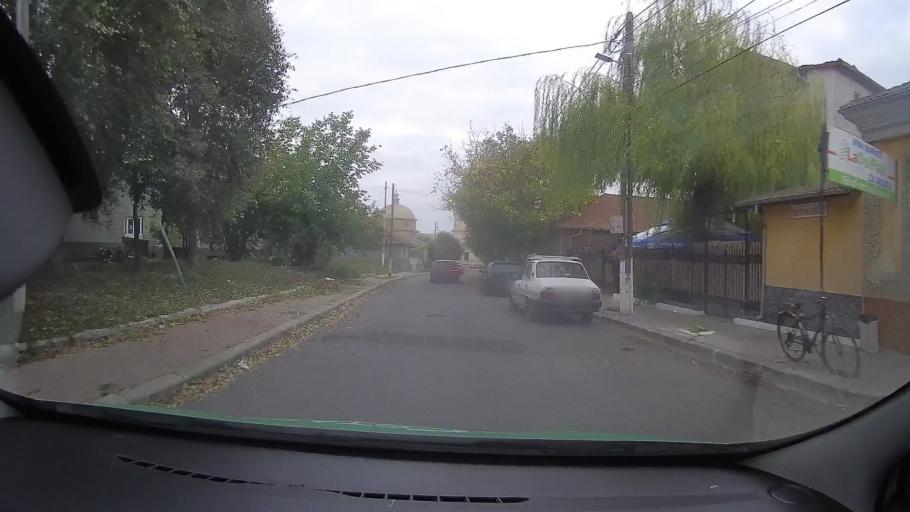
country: RO
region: Tulcea
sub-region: Comuna Jurilovca
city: Jurilovca
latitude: 44.7576
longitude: 28.8758
